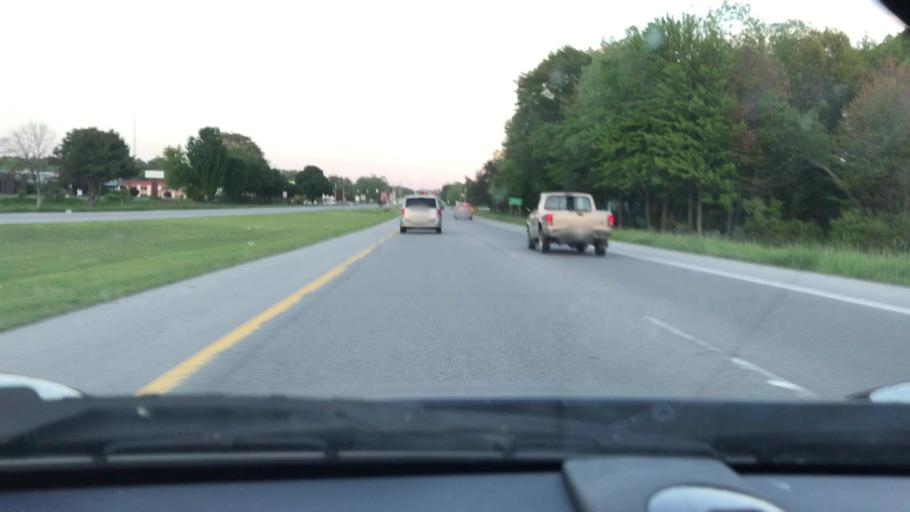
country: US
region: Michigan
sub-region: Muskegon County
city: Muskegon Heights
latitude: 43.1893
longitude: -86.2452
